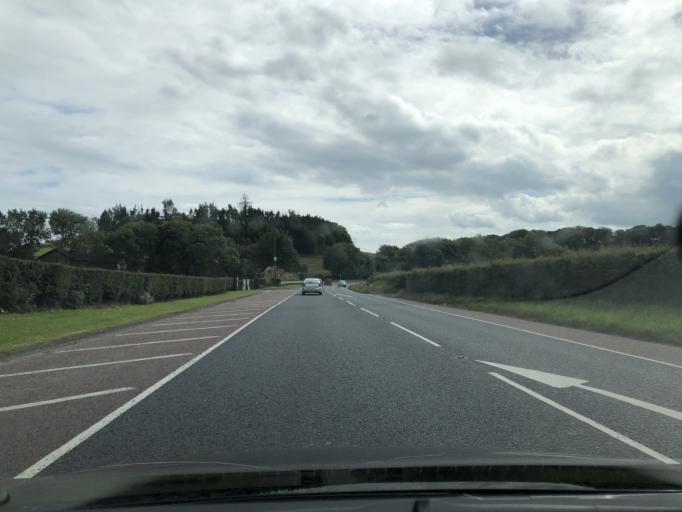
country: GB
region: Northern Ireland
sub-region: Down District
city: Dundrum
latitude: 54.3265
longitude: -5.8350
